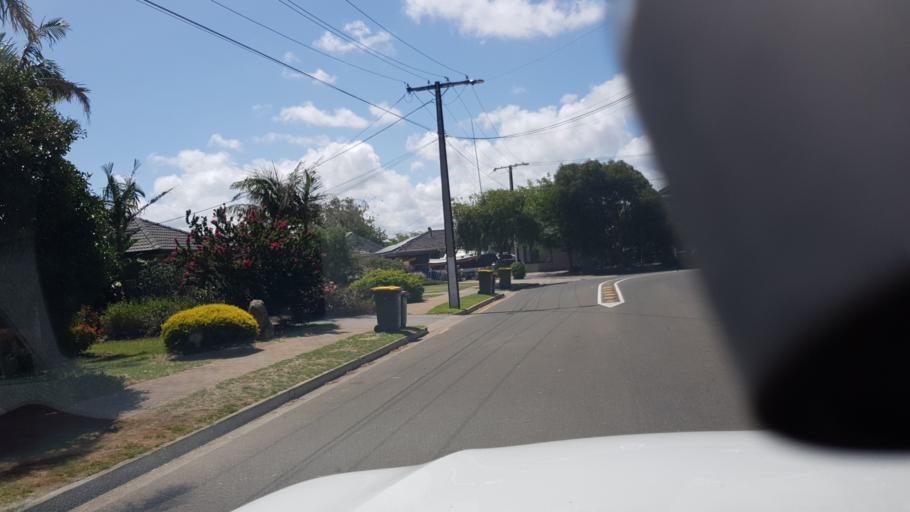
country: AU
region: South Australia
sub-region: Adelaide
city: Brighton
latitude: -35.0105
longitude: 138.5290
